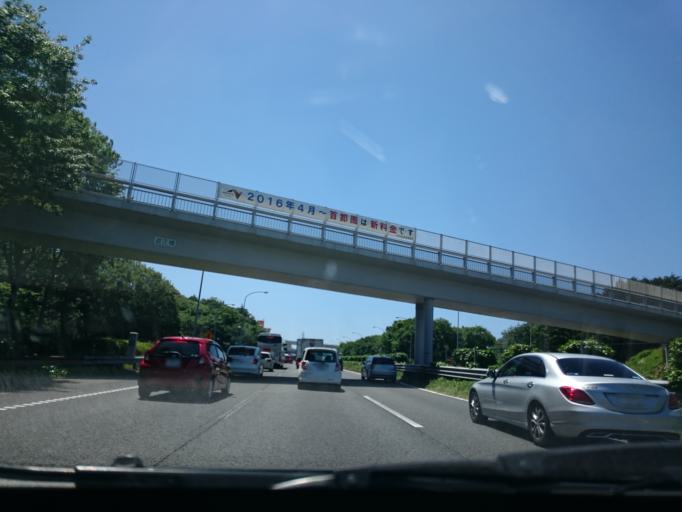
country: JP
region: Kanagawa
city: Minami-rinkan
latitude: 35.5098
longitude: 139.4856
